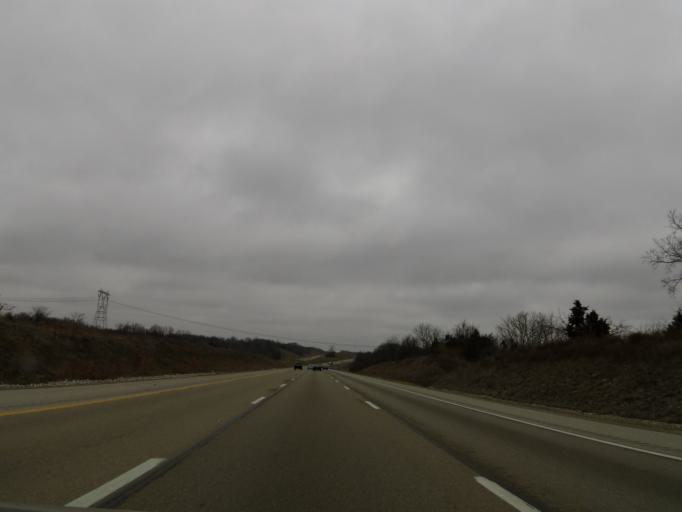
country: US
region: Kentucky
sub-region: Grant County
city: Williamstown
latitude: 38.5909
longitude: -84.5851
